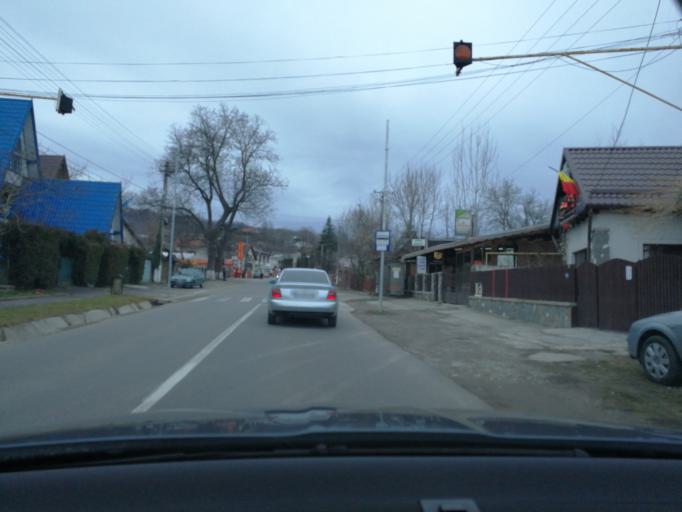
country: RO
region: Prahova
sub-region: Comuna Cornu
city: Cornu de Jos
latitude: 45.1489
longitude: 25.6909
